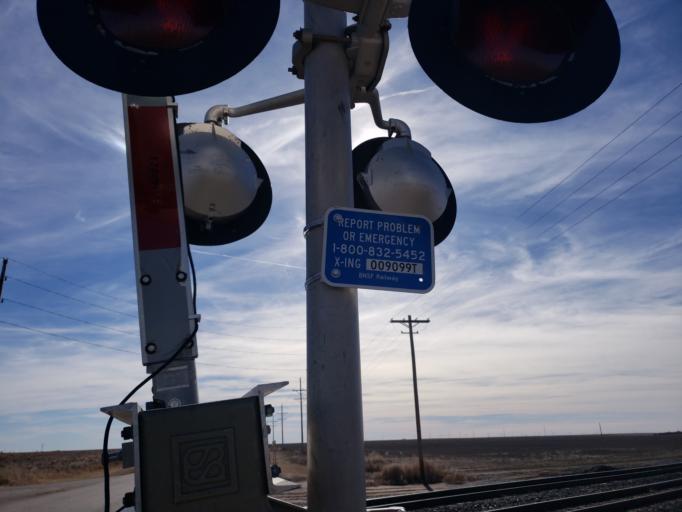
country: US
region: Kansas
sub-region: Ford County
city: Dodge City
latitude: 37.7750
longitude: -99.9060
